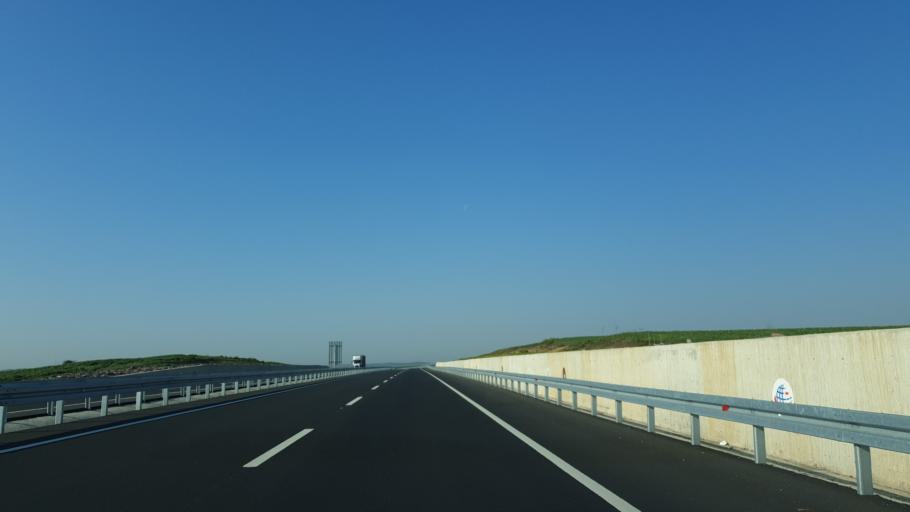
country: TR
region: Tekirdag
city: Marmaracik
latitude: 41.1958
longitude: 27.7525
